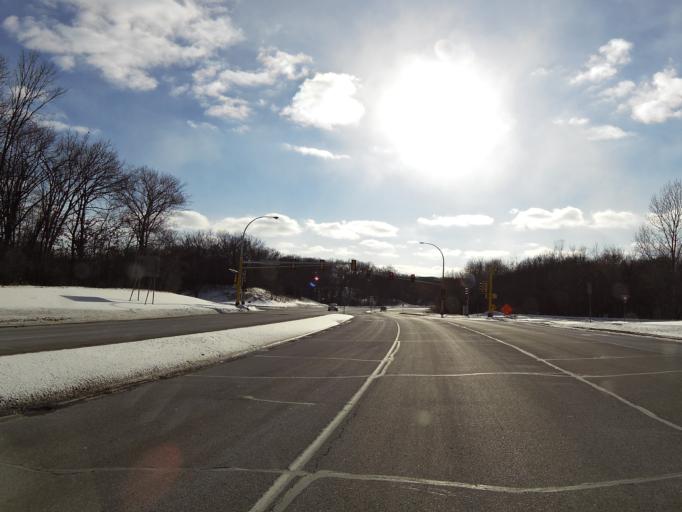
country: US
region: Minnesota
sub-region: Dakota County
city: Apple Valley
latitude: 44.7593
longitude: -93.2223
